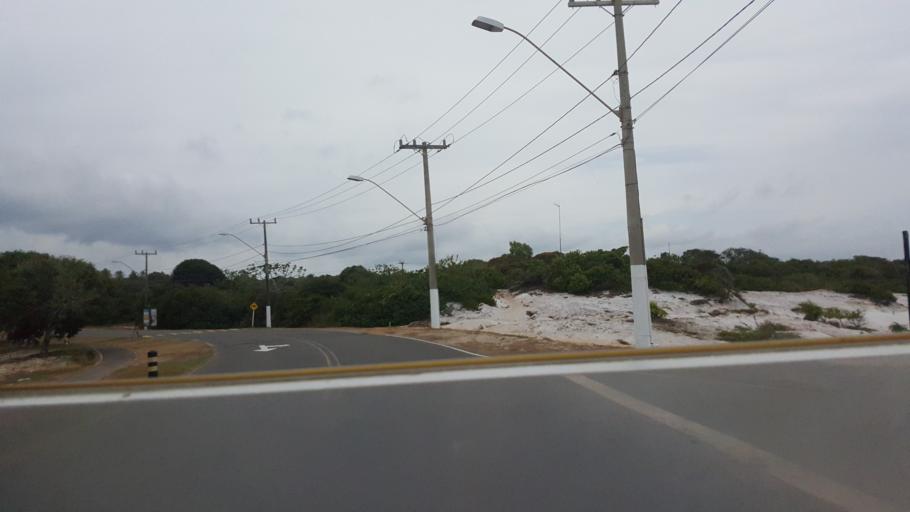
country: BR
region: Bahia
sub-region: Mata De Sao Joao
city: Mata de Sao Joao
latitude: -12.4305
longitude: -37.9188
